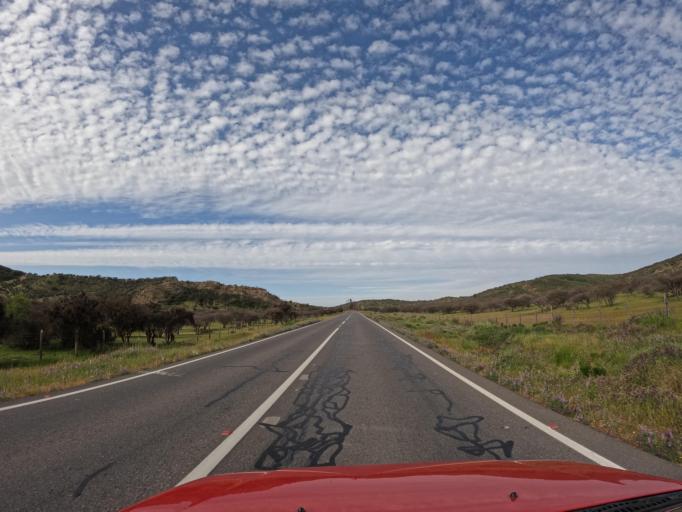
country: CL
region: O'Higgins
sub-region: Provincia de Colchagua
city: Santa Cruz
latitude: -34.3140
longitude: -71.7408
